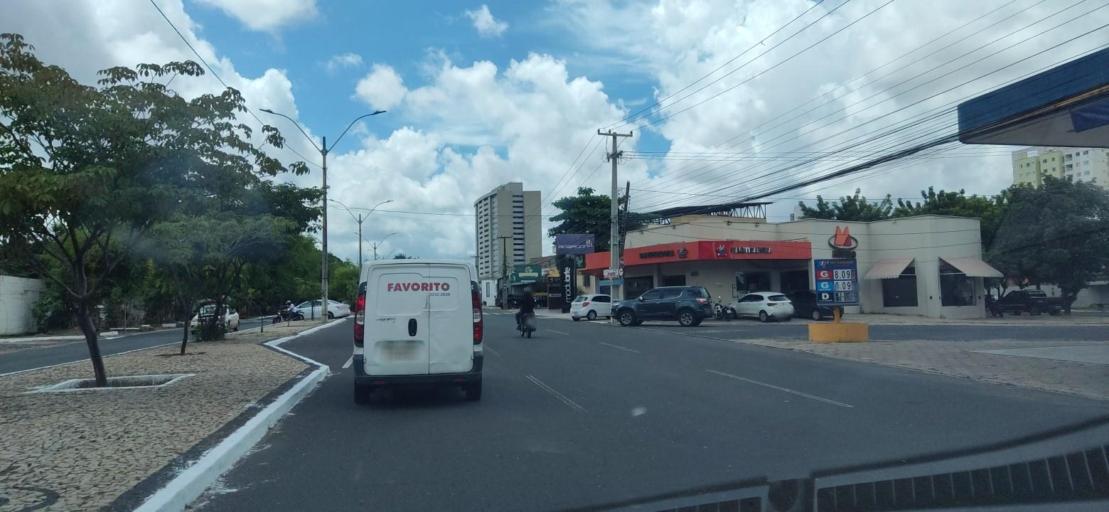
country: BR
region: Piaui
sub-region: Teresina
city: Teresina
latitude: -5.0624
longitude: -42.8004
